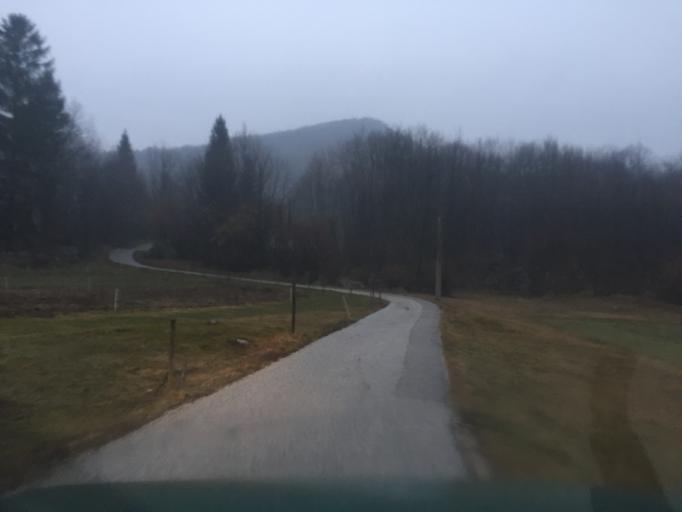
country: SI
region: Kanal
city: Kanal
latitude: 46.0512
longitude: 13.6659
